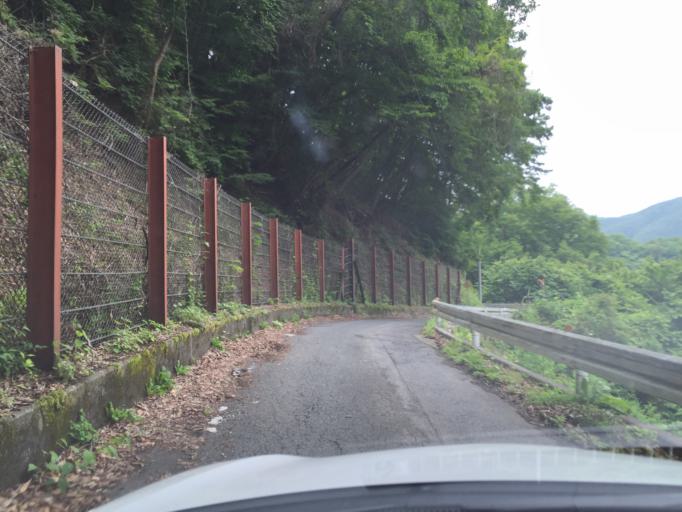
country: JP
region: Fukushima
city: Iwaki
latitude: 37.2079
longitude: 140.7226
